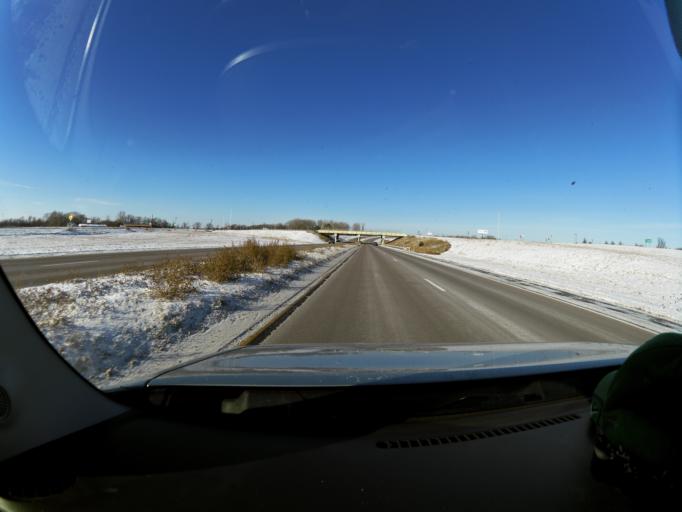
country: US
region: Minnesota
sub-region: Goodhue County
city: Cannon Falls
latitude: 44.5995
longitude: -92.9924
